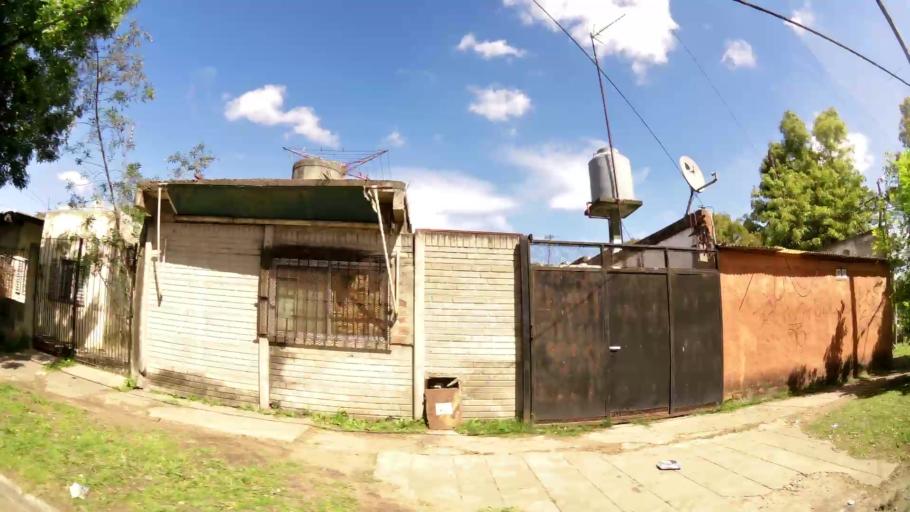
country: AR
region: Buenos Aires
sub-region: Partido de Quilmes
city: Quilmes
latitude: -34.8184
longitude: -58.2613
